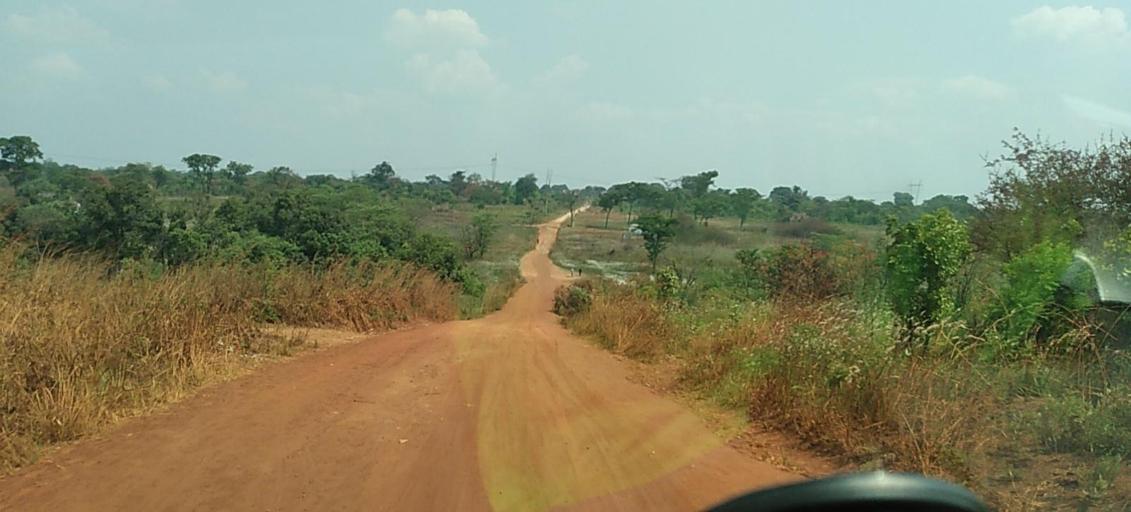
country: ZM
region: North-Western
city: Solwezi
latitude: -12.1107
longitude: 26.3668
